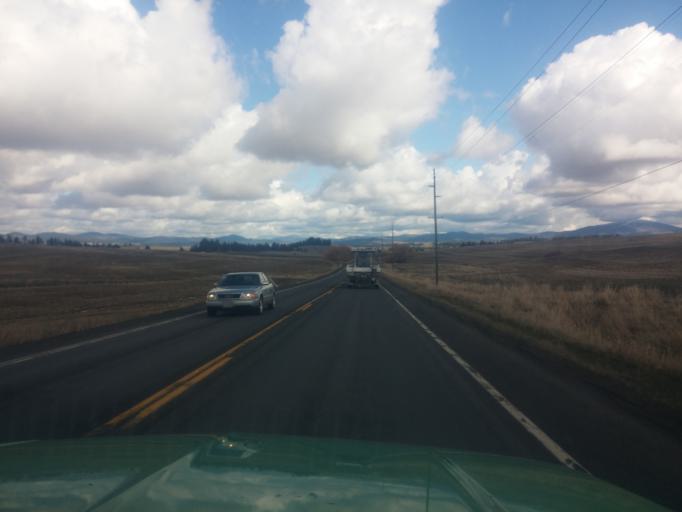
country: US
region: Idaho
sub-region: Latah County
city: Moscow
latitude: 46.8896
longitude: -116.9971
